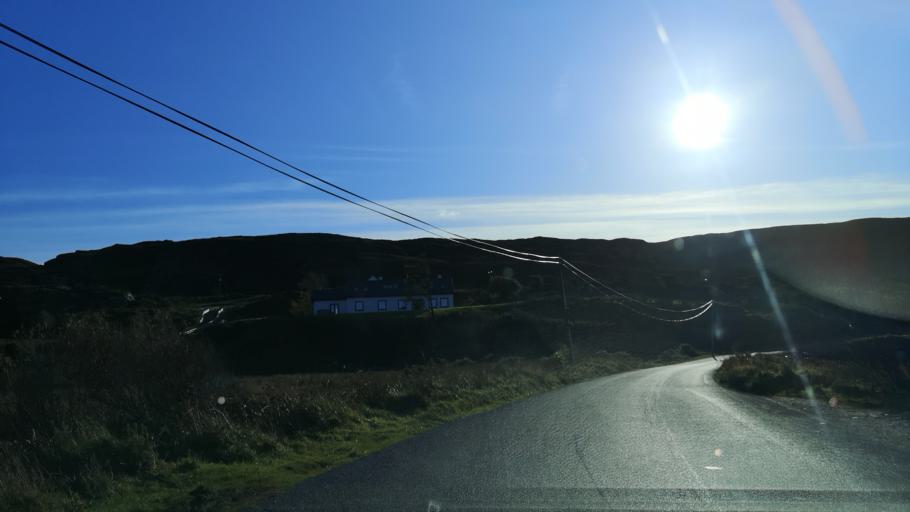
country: IE
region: Connaught
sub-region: County Galway
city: Clifden
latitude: 53.5046
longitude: -10.0518
